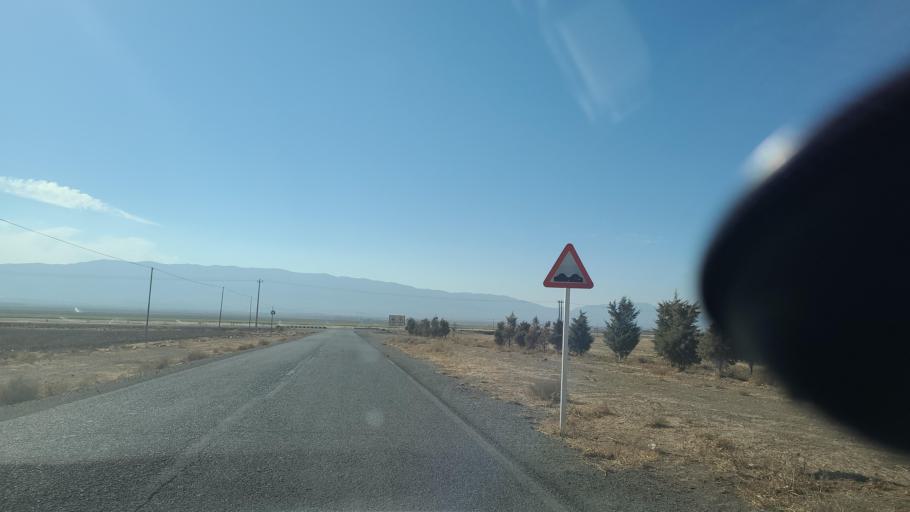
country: IR
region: Razavi Khorasan
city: Dowlatabad
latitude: 35.6017
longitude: 59.4609
